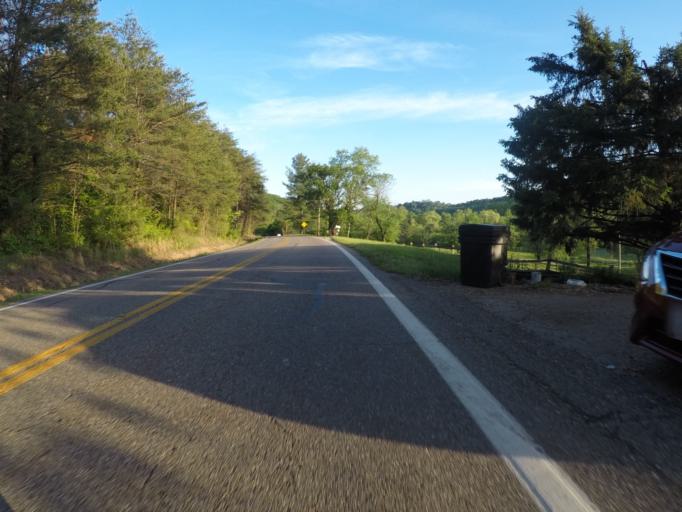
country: US
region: West Virginia
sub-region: Cabell County
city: Huntington
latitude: 38.5046
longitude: -82.4776
